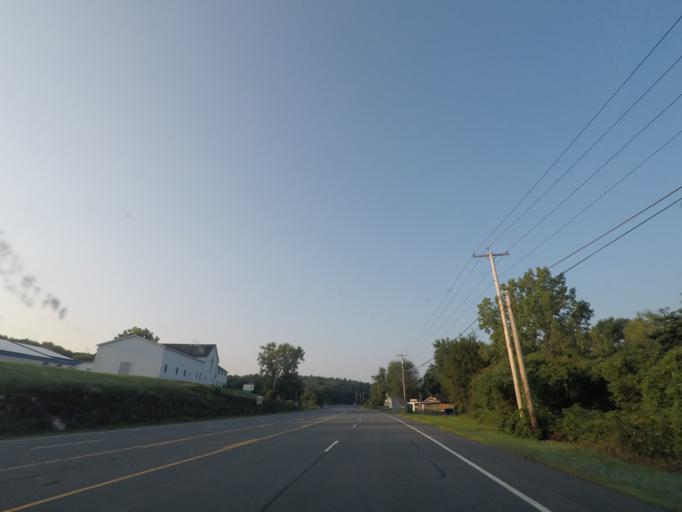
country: US
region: New York
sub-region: Rensselaer County
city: East Greenbush
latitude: 42.5349
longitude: -73.6791
